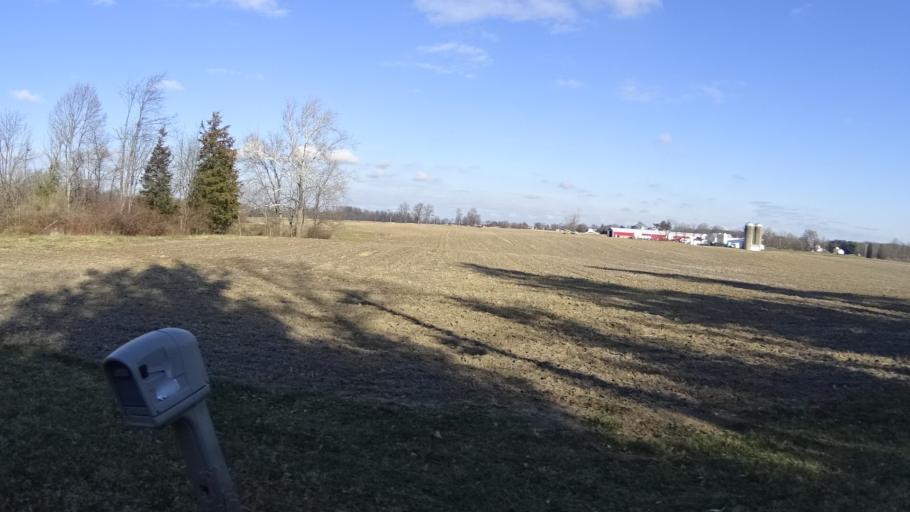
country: US
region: Ohio
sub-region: Lorain County
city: Wellington
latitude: 41.2235
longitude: -82.2227
